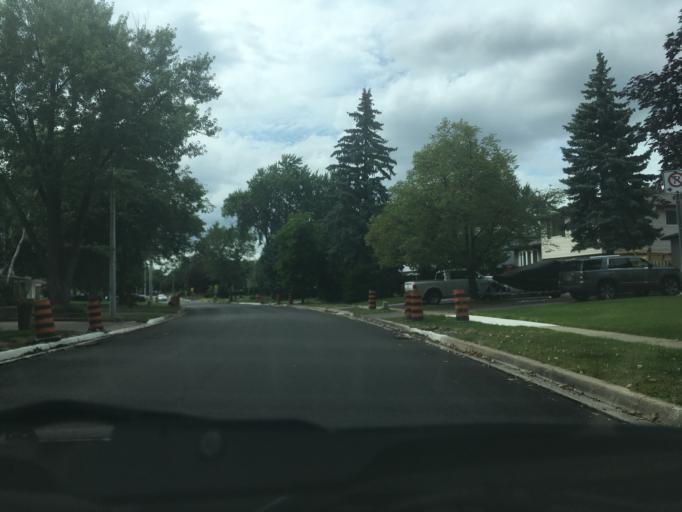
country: CA
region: Ontario
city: Brampton
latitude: 43.6729
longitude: -79.7352
